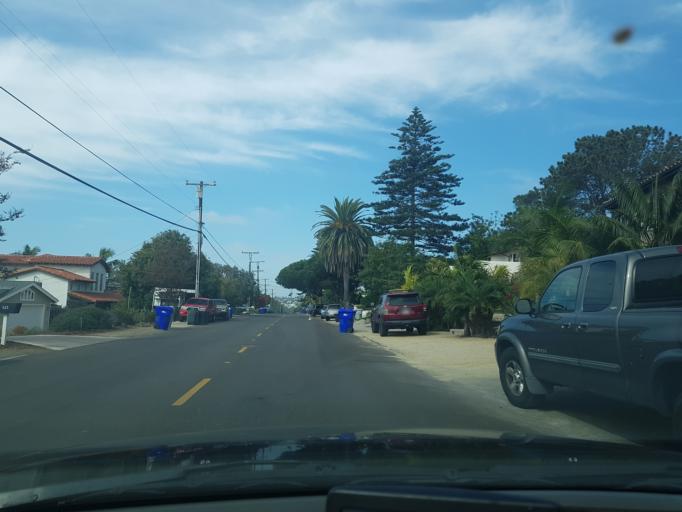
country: US
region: California
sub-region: San Diego County
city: Solana Beach
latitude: 32.9983
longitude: -117.2710
